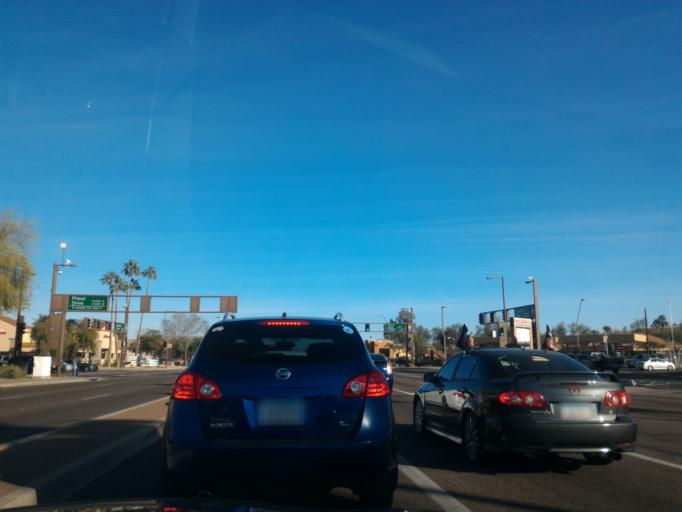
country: US
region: Arizona
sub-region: Maricopa County
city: Guadalupe
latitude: 33.3783
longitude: -111.9639
